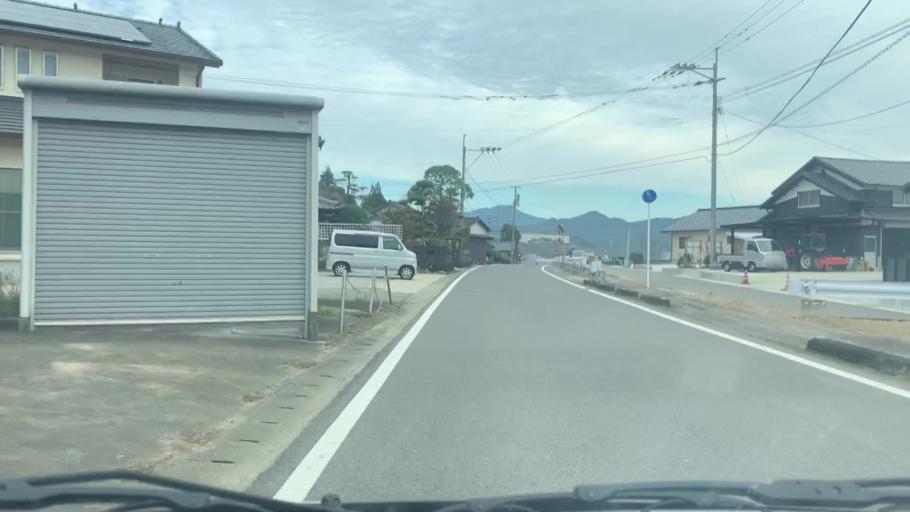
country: JP
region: Saga Prefecture
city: Takeocho-takeo
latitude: 33.2014
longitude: 129.9610
